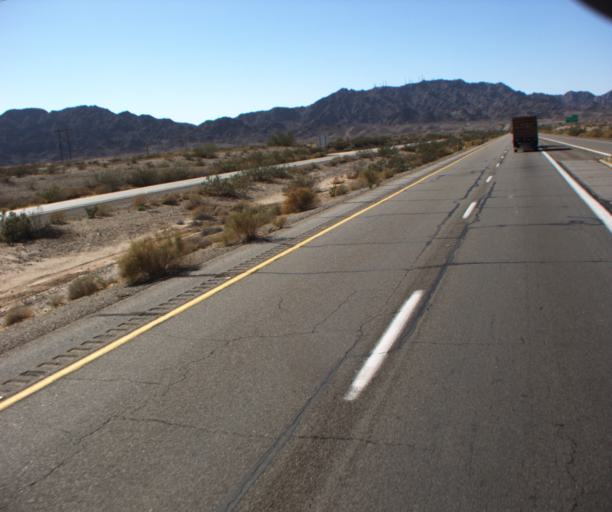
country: US
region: Arizona
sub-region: Yuma County
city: Fortuna Foothills
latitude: 32.6673
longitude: -114.2840
